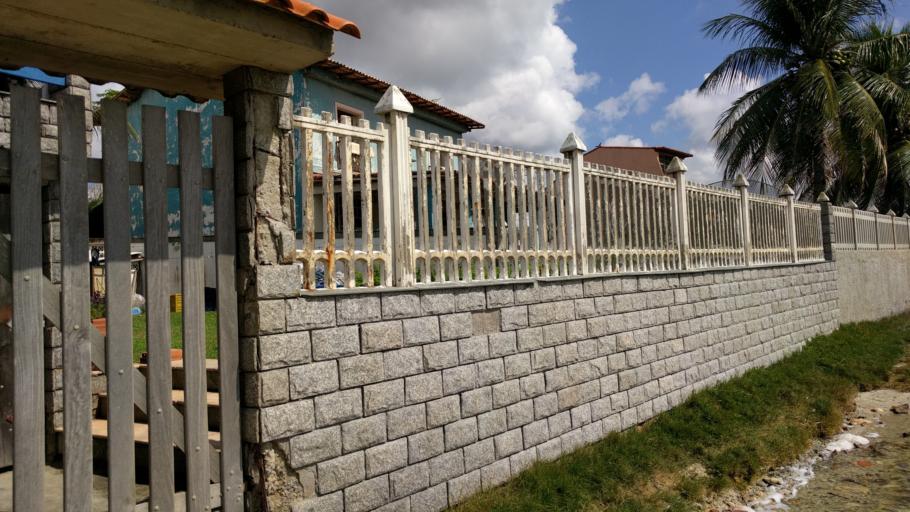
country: BR
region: Rio de Janeiro
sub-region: Sao Pedro Da Aldeia
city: Sao Pedro da Aldeia
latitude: -22.8419
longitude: -42.1262
